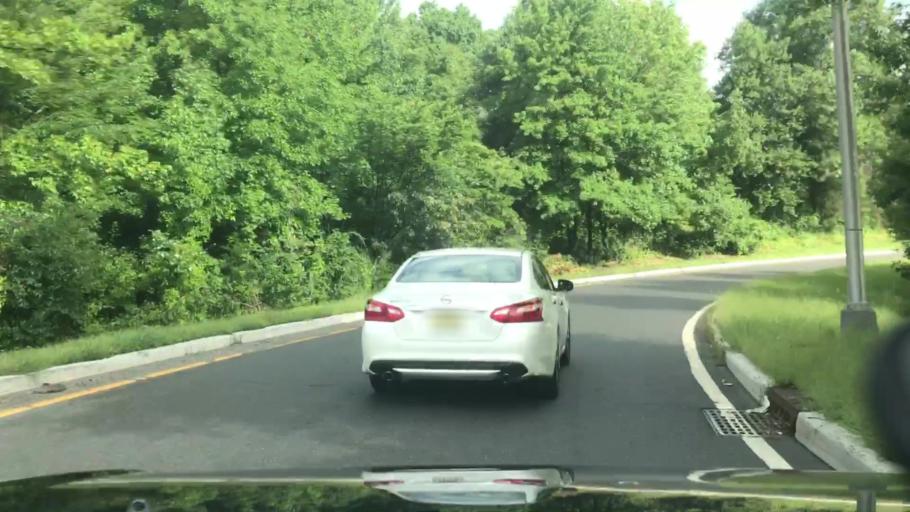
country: US
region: New Jersey
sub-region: Middlesex County
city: Fords
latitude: 40.5204
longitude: -74.3044
